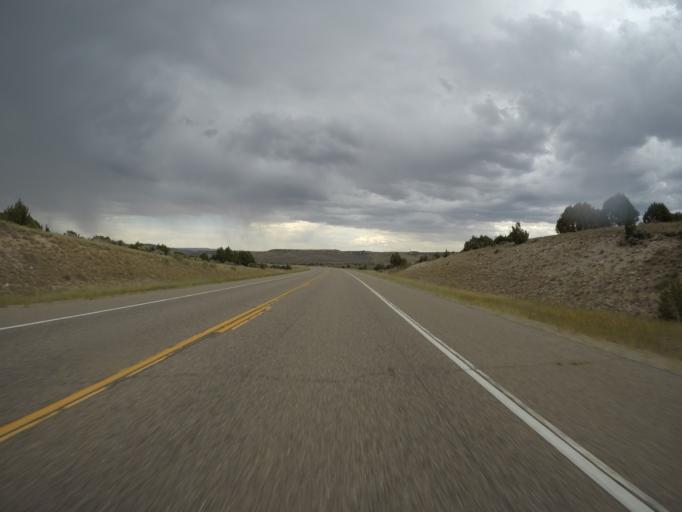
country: US
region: Colorado
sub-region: Rio Blanco County
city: Rangely
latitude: 40.3858
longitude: -108.3502
